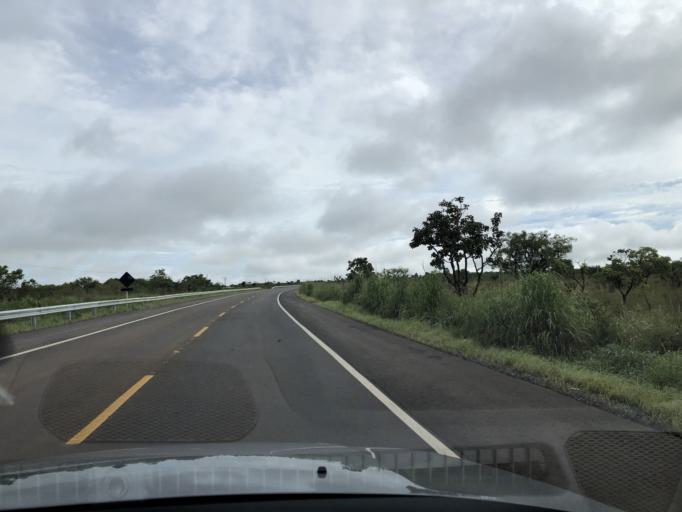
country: BR
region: Federal District
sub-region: Brasilia
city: Brasilia
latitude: -15.6312
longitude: -48.0762
